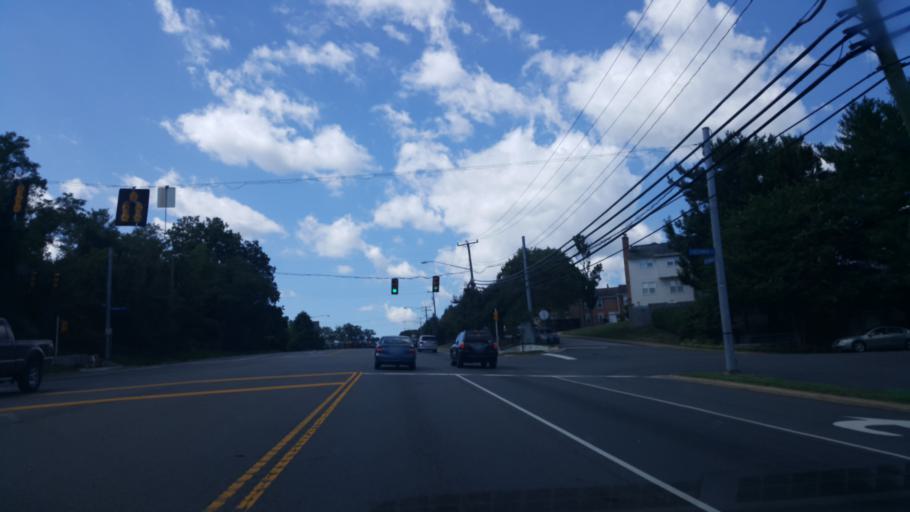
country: US
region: Virginia
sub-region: Fairfax County
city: Lorton
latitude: 38.7003
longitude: -77.2111
